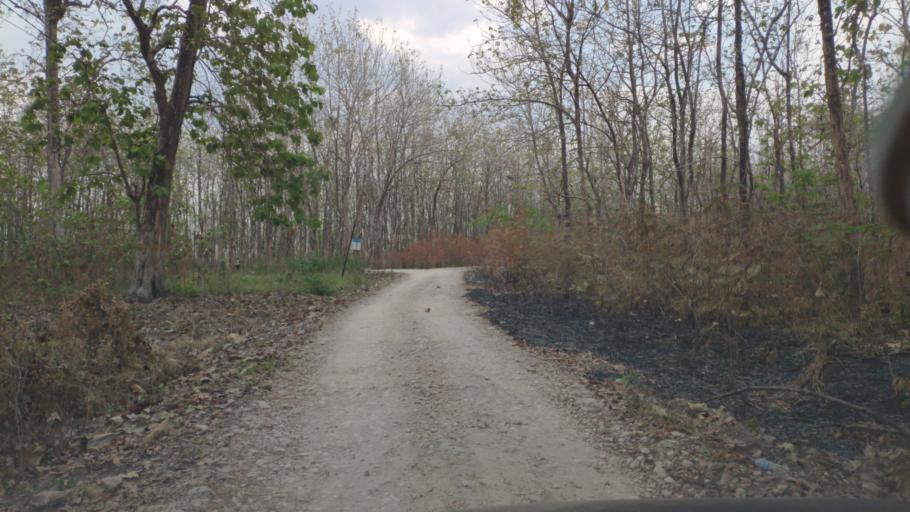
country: ID
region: Central Java
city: Randublatung
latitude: -7.3038
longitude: 111.3506
